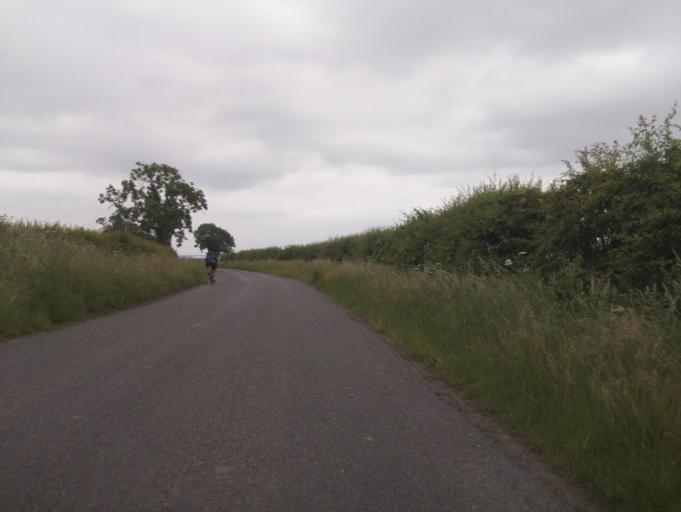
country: GB
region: England
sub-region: District of Rutland
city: Langham
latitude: 52.6700
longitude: -0.7606
